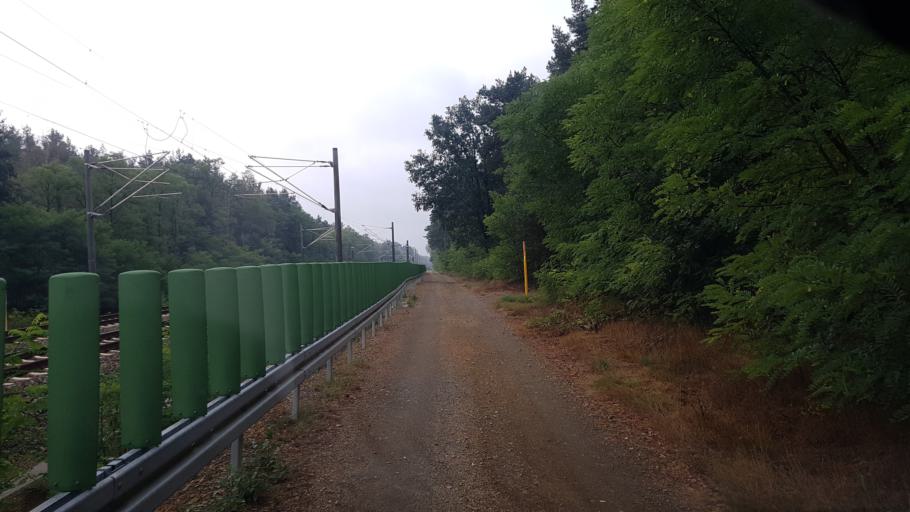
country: DE
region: Brandenburg
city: Ruckersdorf
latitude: 51.5483
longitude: 13.5755
